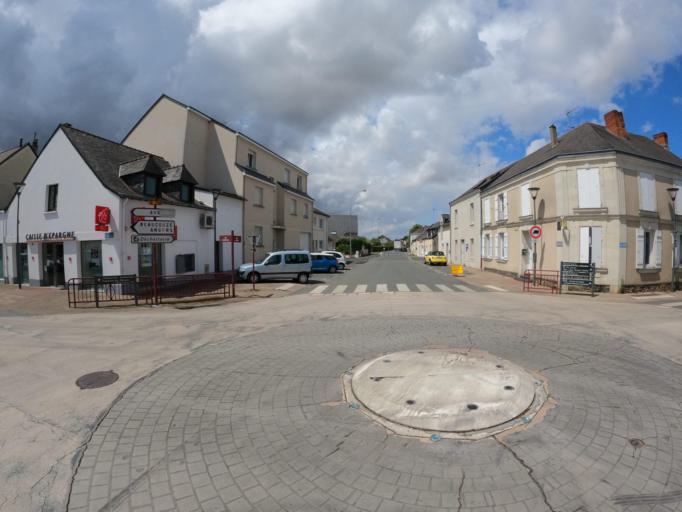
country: FR
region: Pays de la Loire
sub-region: Departement de Maine-et-Loire
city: Avrille
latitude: 47.5288
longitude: -0.6118
